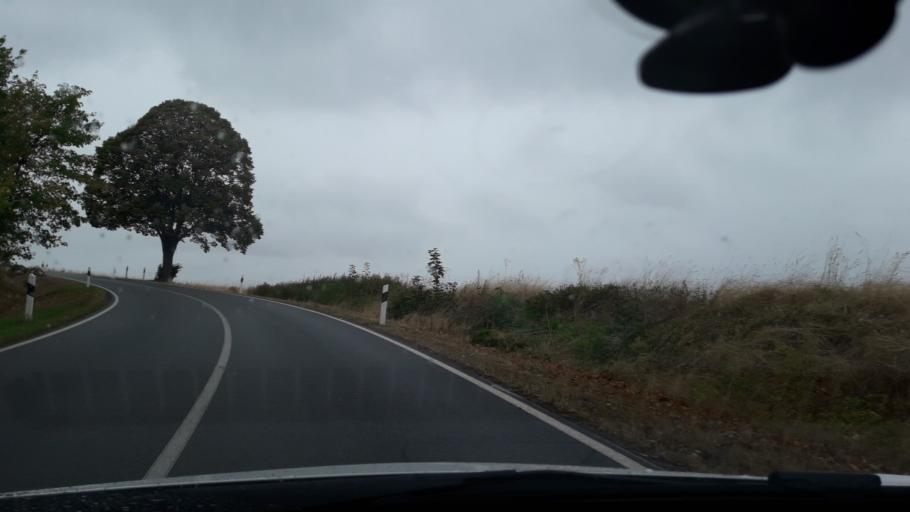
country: DE
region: Lower Saxony
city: Vienenburg
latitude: 51.9676
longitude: 10.5780
